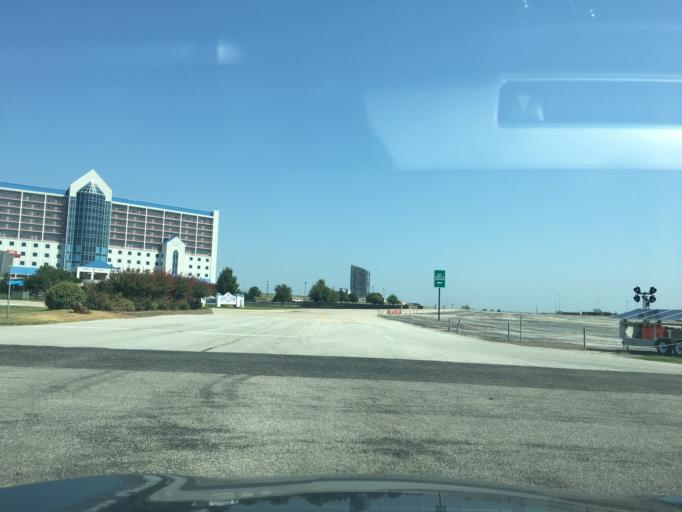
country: US
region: Texas
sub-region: Denton County
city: Justin
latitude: 33.0300
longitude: -97.2788
